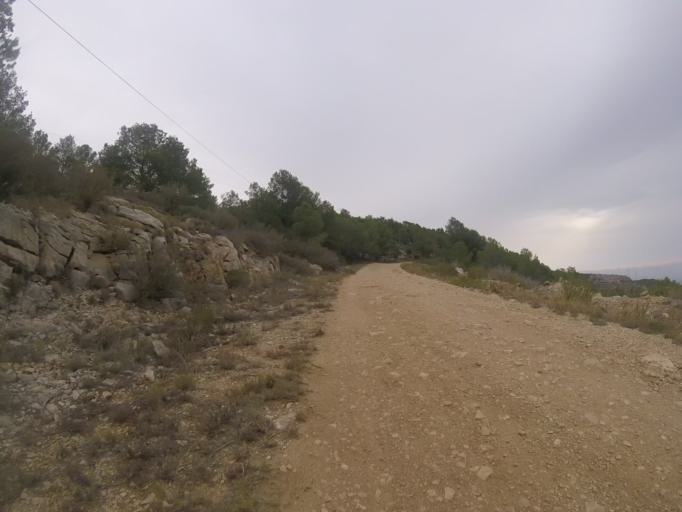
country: ES
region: Valencia
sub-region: Provincia de Castello
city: Alcoceber
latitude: 40.2759
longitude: 0.2804
